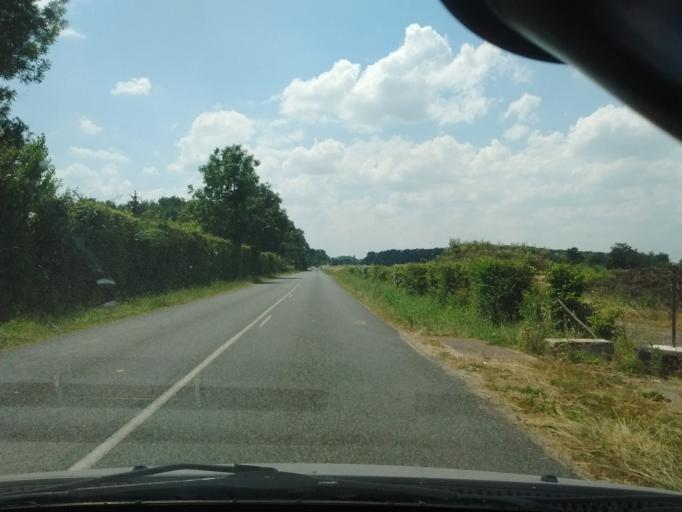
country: FR
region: Ile-de-France
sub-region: Departement de Seine-et-Marne
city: Ponthierry
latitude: 48.5153
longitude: 2.5395
